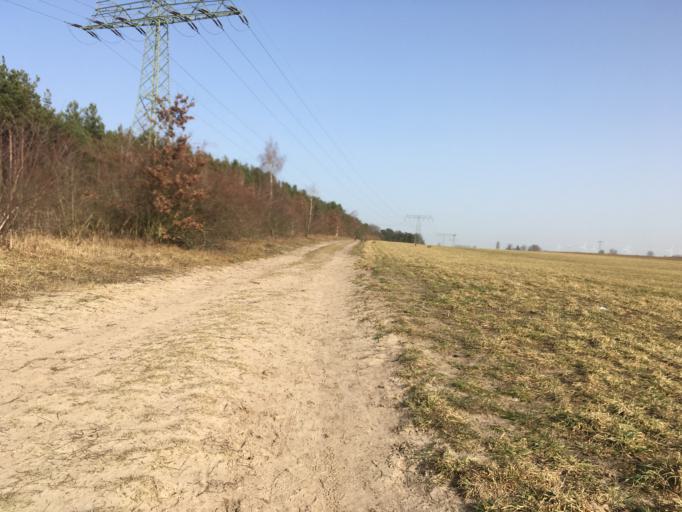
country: DE
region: Brandenburg
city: Bernau bei Berlin
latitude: 52.6834
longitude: 13.5341
